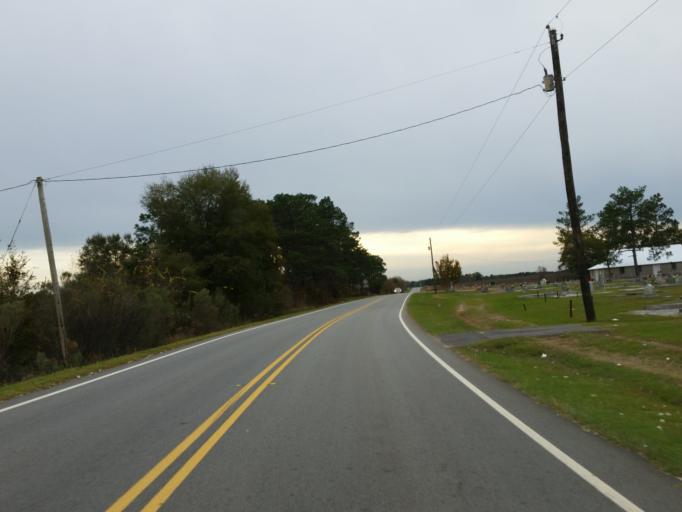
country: US
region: Georgia
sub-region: Crisp County
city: Cordele
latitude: 31.8541
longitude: -83.7445
